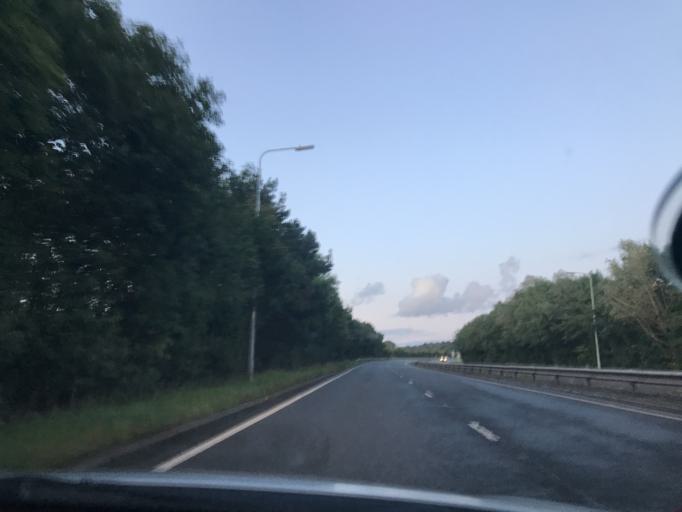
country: GB
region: England
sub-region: Cheshire West and Chester
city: Kelsall
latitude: 53.2112
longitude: -2.7281
